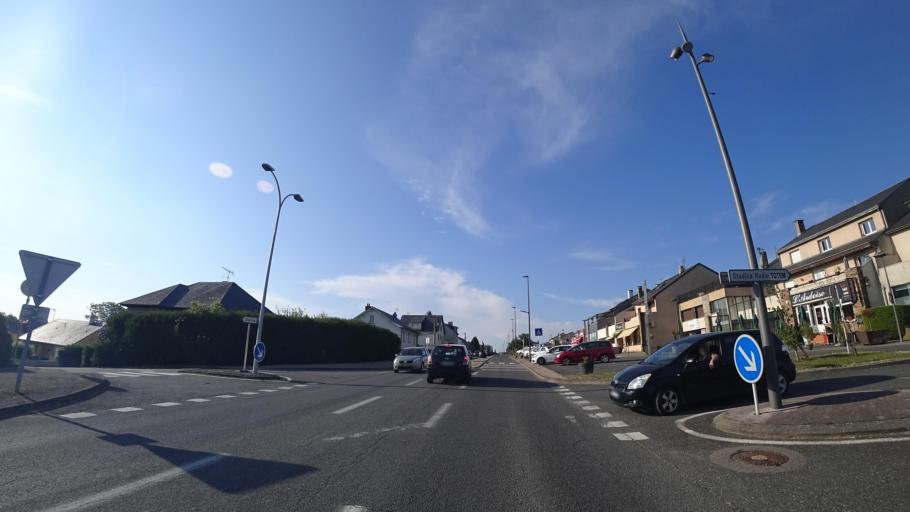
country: FR
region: Midi-Pyrenees
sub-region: Departement de l'Aveyron
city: Luc-la-Primaube
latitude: 44.2973
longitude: 2.5577
